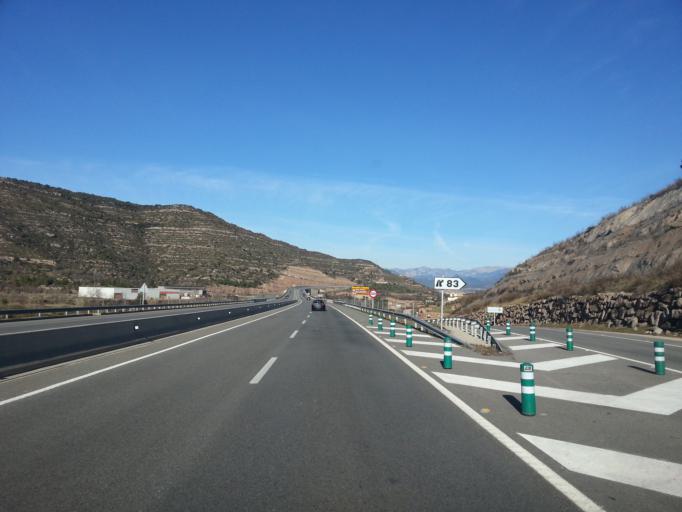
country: ES
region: Catalonia
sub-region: Provincia de Barcelona
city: Puig-reig
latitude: 41.9783
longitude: 1.8873
